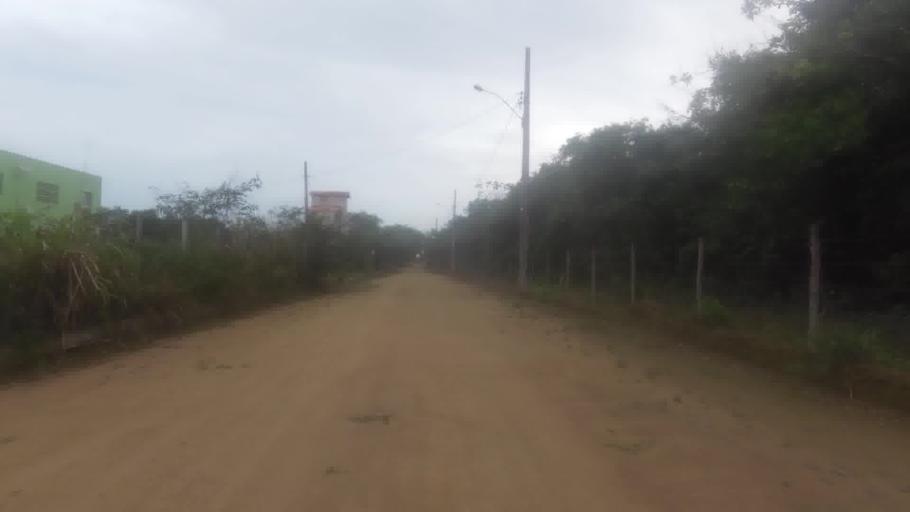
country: BR
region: Espirito Santo
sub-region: Piuma
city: Piuma
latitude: -20.7950
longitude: -40.5867
